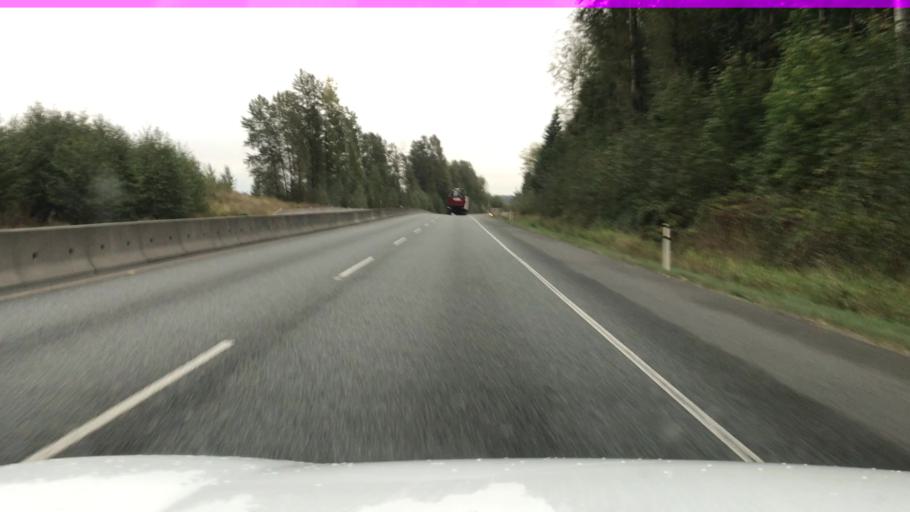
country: CA
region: British Columbia
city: Coquitlam
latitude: 49.2119
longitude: -122.7921
